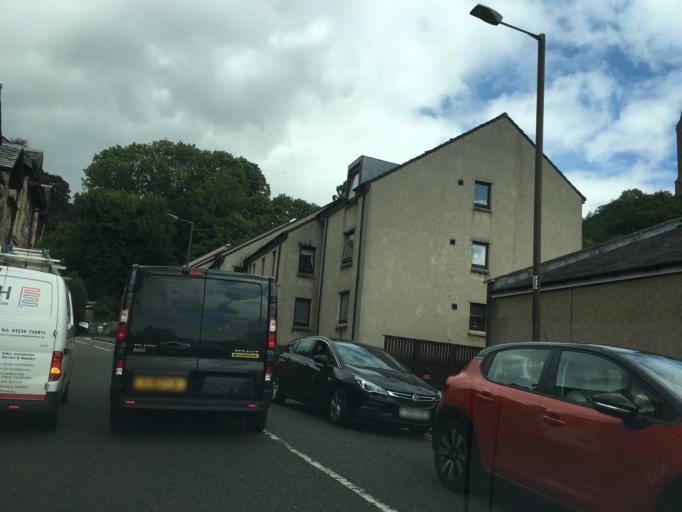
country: GB
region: Scotland
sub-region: Stirling
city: Stirling
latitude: 56.1386
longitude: -3.9234
